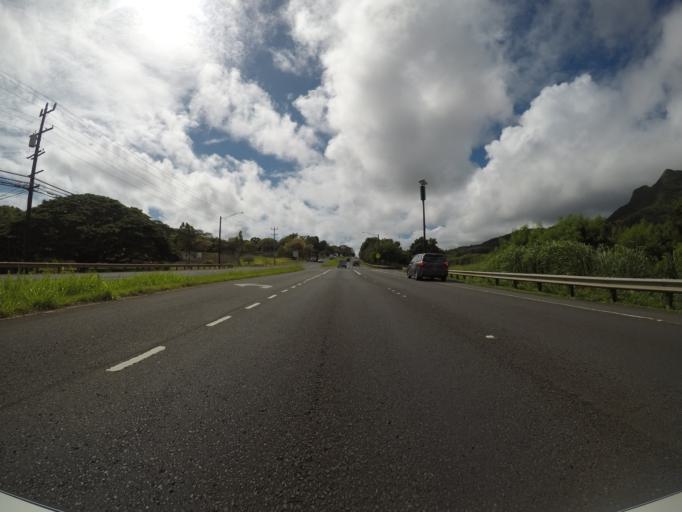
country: US
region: Hawaii
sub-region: Honolulu County
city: Maunawili
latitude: 21.3769
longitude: -157.7493
